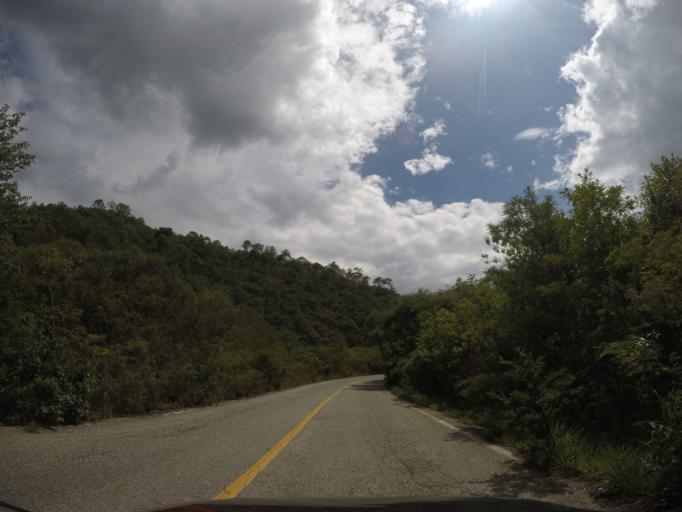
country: MX
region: Oaxaca
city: San Francisco Sola
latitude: 16.4321
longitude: -97.0378
